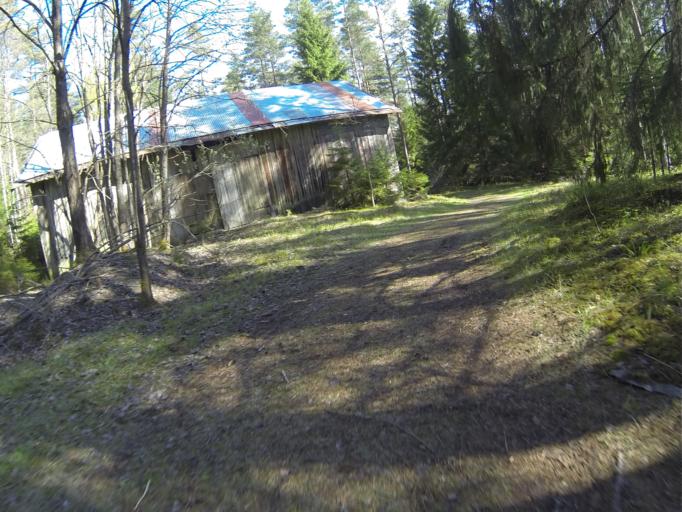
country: FI
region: Varsinais-Suomi
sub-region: Salo
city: Pertteli
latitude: 60.3955
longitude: 23.2126
